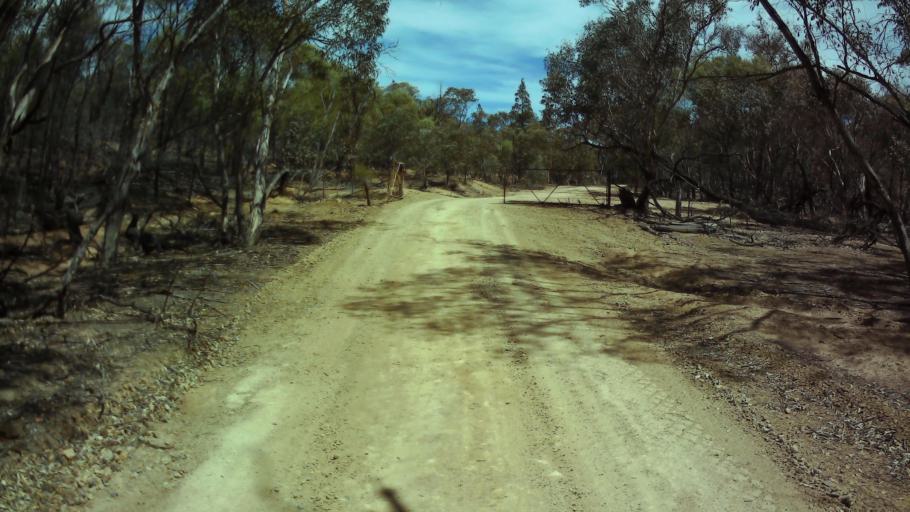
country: AU
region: New South Wales
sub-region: Weddin
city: Grenfell
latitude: -33.8047
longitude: 148.1606
